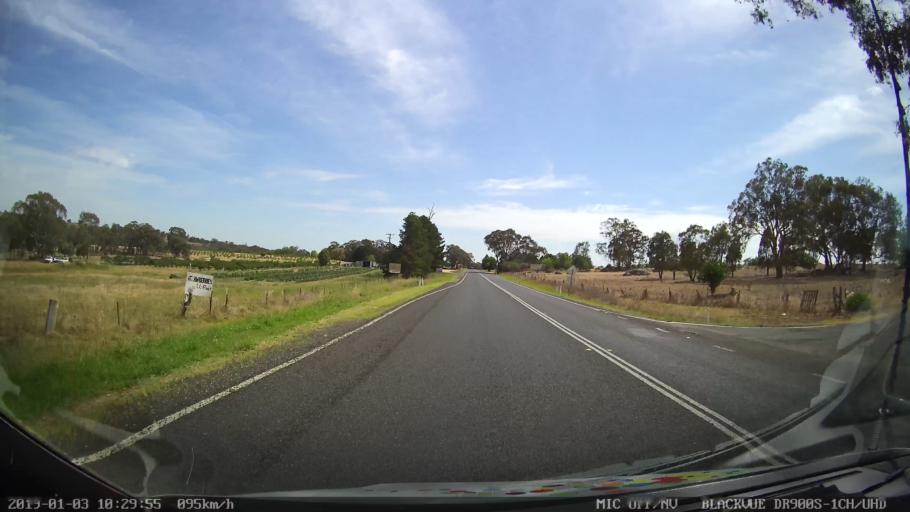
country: AU
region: New South Wales
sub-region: Young
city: Young
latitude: -34.3680
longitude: 148.2626
